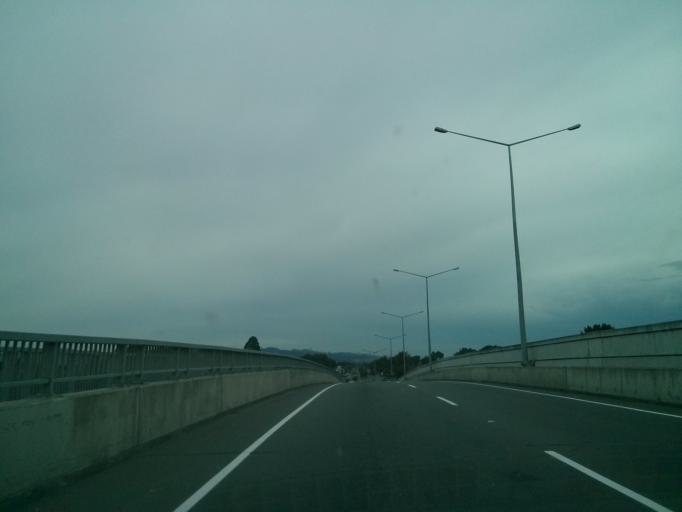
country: NZ
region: Canterbury
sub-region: Christchurch City
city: Christchurch
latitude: -43.4693
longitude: 172.6175
